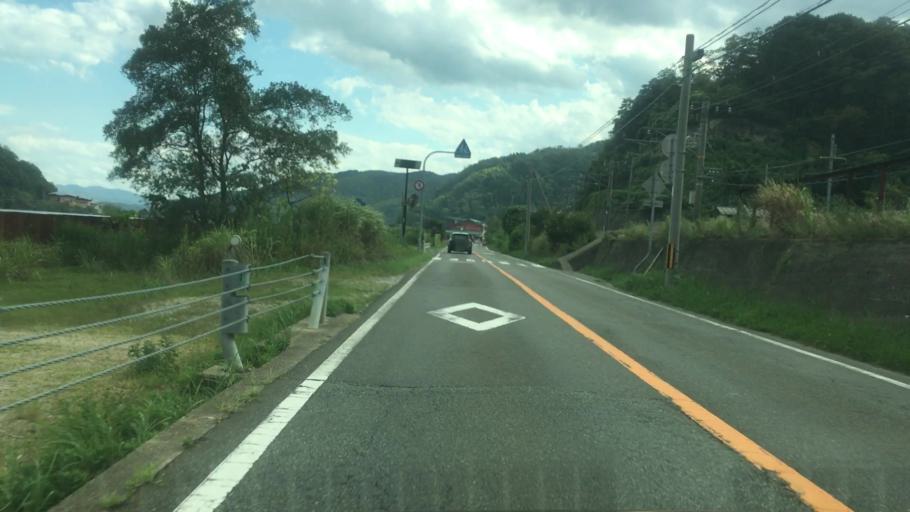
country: JP
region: Hyogo
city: Toyooka
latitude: 35.5966
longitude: 134.8016
